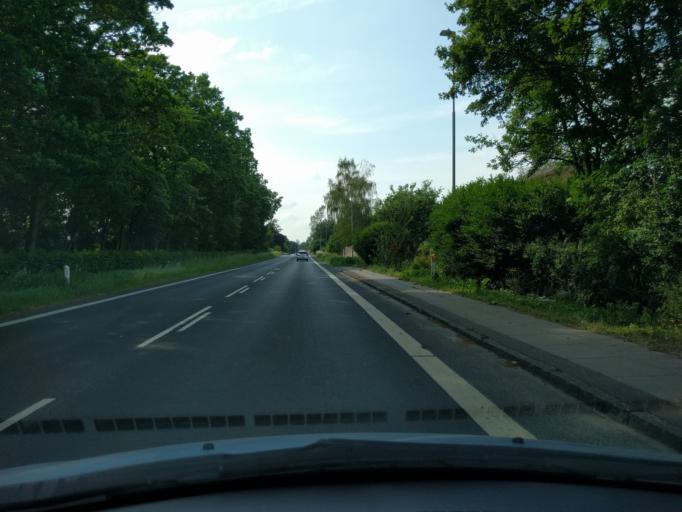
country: DK
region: South Denmark
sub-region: Odense Kommune
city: Odense
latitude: 55.4133
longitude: 10.3245
